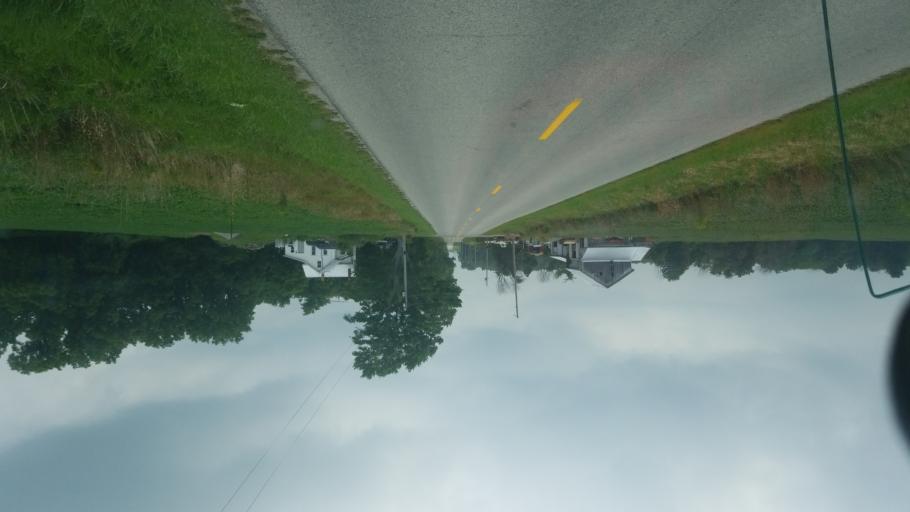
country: US
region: Ohio
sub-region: Huron County
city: Greenwich
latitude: 41.0828
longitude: -82.5645
